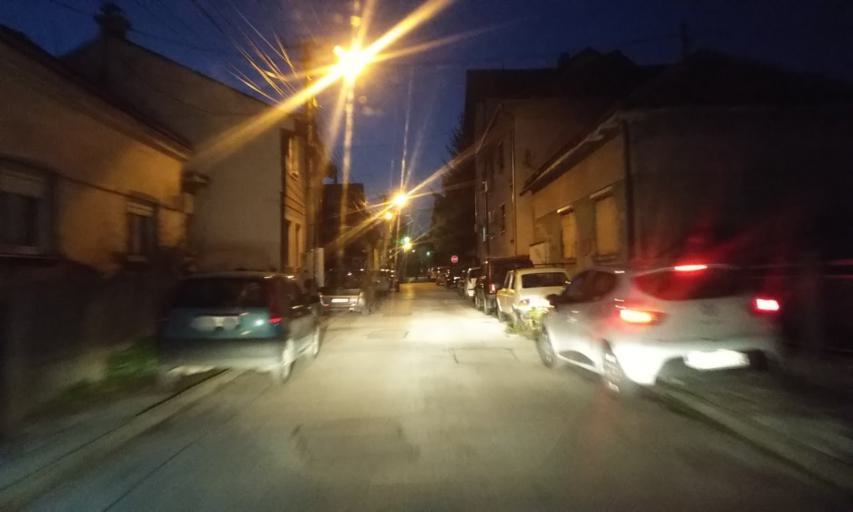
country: RS
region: Central Serbia
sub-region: Nisavski Okrug
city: Nis
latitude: 43.3299
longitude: 21.9118
